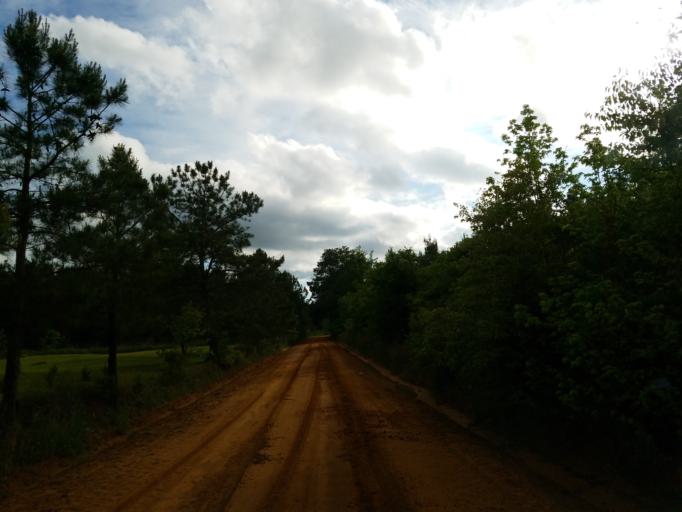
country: US
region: Georgia
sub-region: Dooly County
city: Vienna
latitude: 32.1372
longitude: -83.7925
